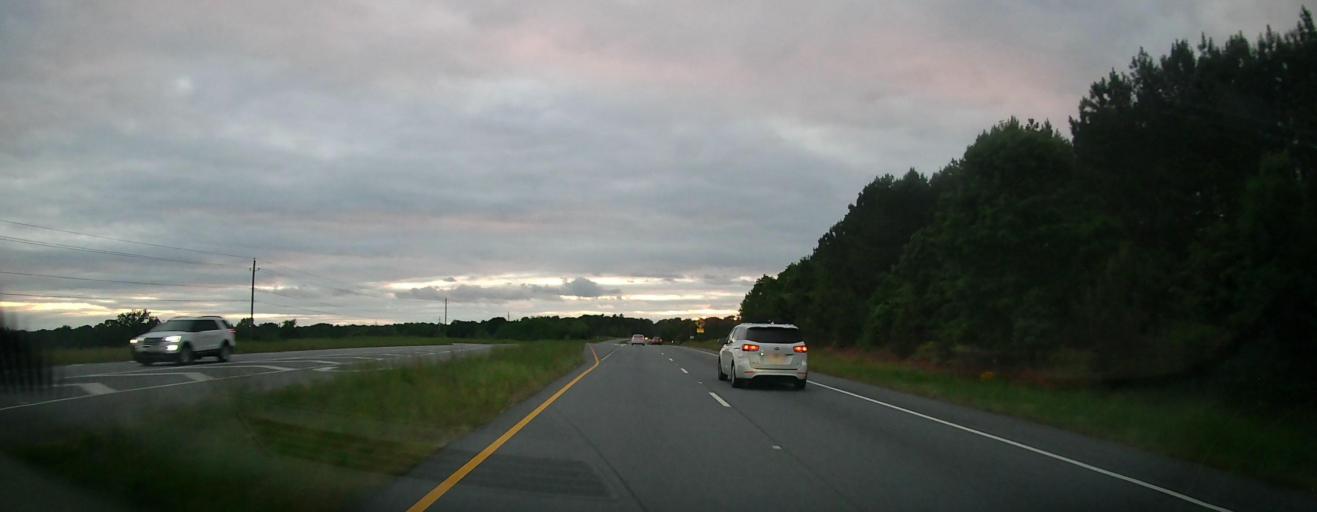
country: US
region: Georgia
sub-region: Jackson County
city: Arcade
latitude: 34.0622
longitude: -83.5255
